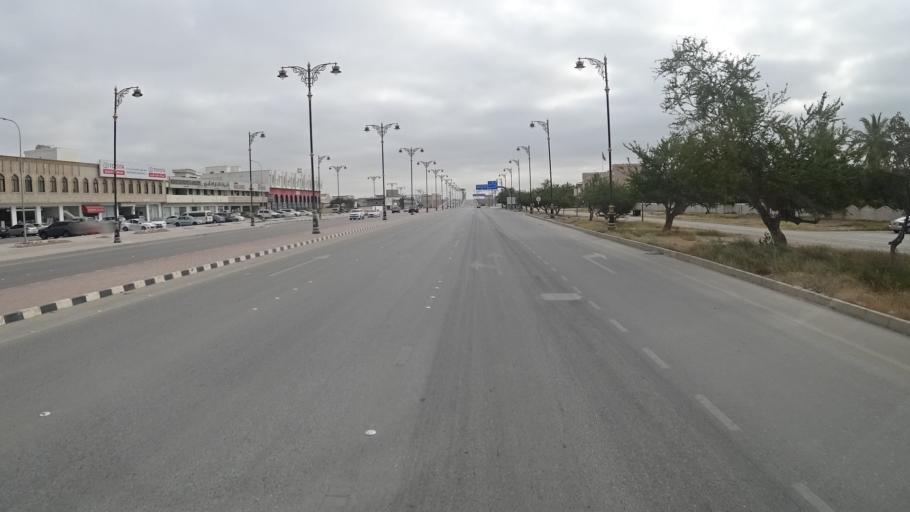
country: OM
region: Zufar
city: Salalah
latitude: 17.0135
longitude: 54.0516
